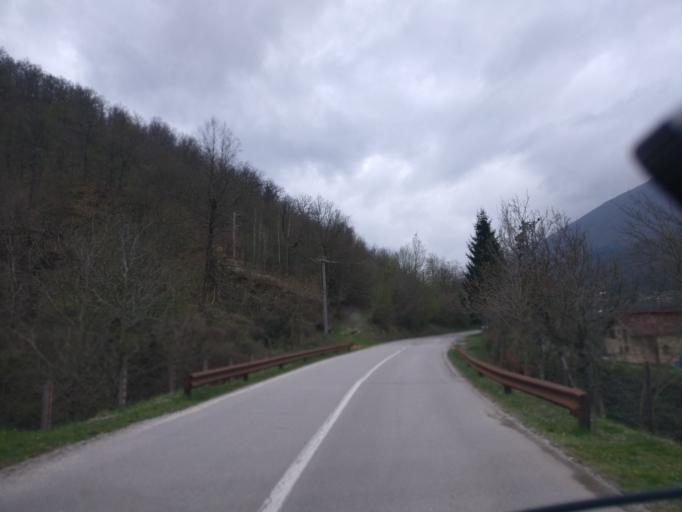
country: BA
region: Republika Srpska
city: Foca
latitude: 43.4505
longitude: 18.7555
